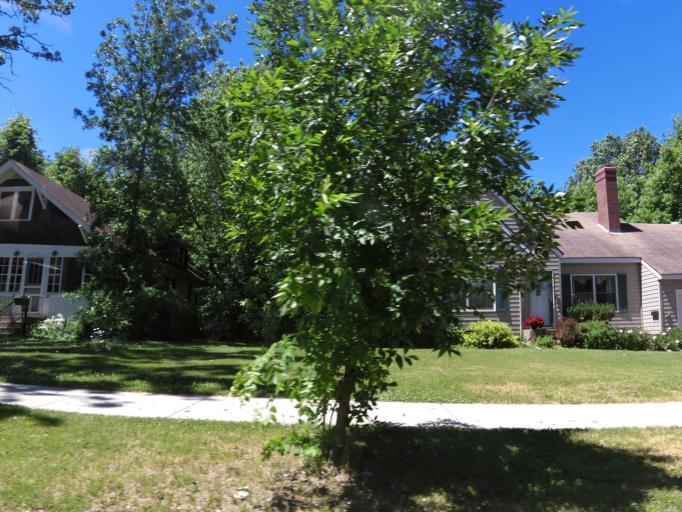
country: US
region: Minnesota
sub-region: Becker County
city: Detroit Lakes
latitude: 46.8110
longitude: -95.8489
